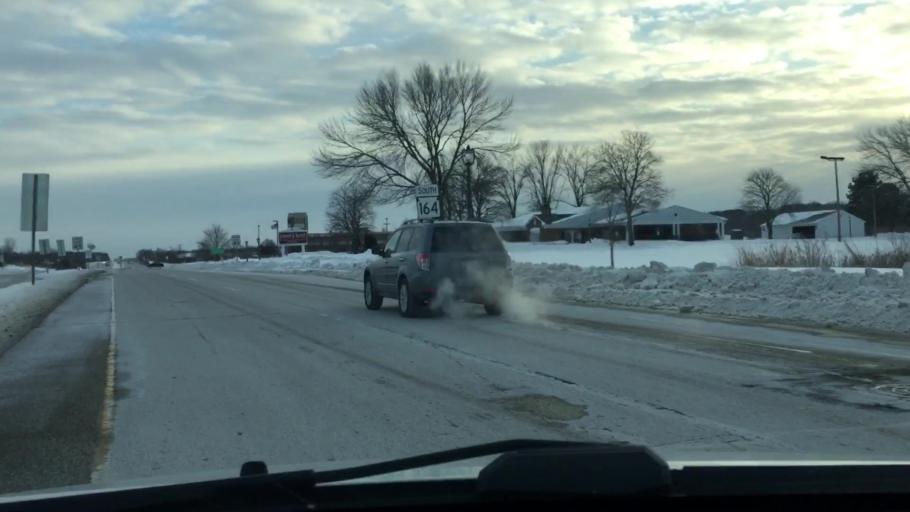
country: US
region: Wisconsin
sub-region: Waukesha County
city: Sussex
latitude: 43.1370
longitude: -88.2440
